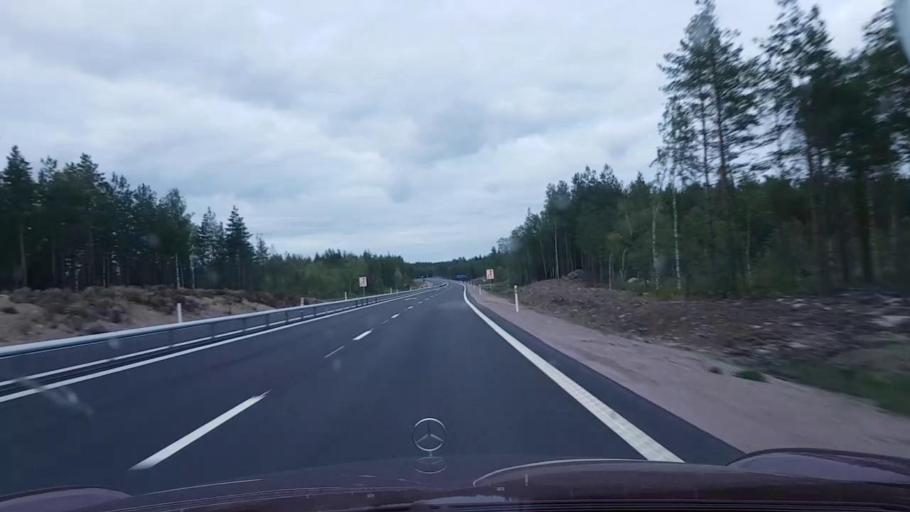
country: SE
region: Vaestmanland
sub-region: Surahammars Kommun
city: Surahammar
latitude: 59.6848
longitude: 16.2436
